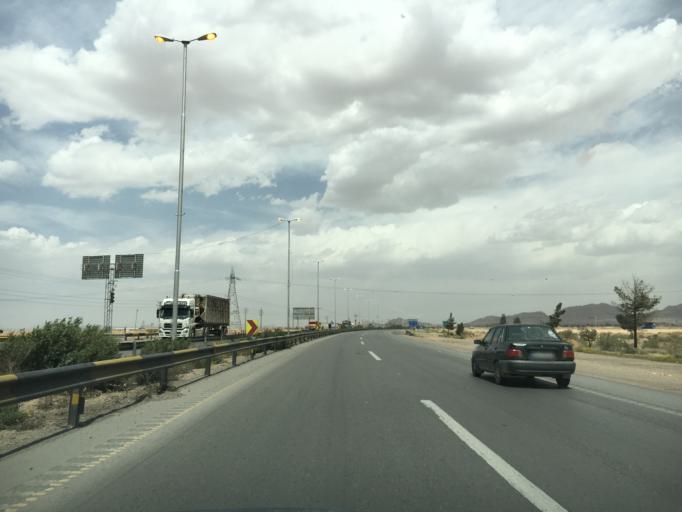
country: IR
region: Isfahan
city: Shahin Shahr
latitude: 32.9319
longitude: 51.5161
